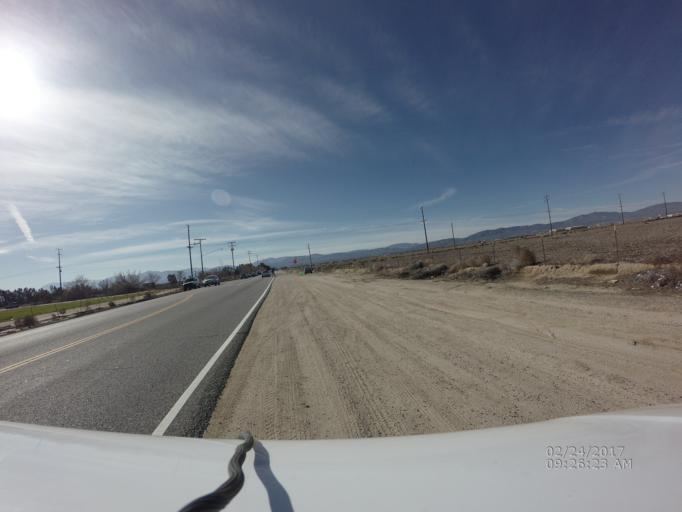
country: US
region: California
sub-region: Los Angeles County
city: Palmdale
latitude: 34.6322
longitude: -118.0410
